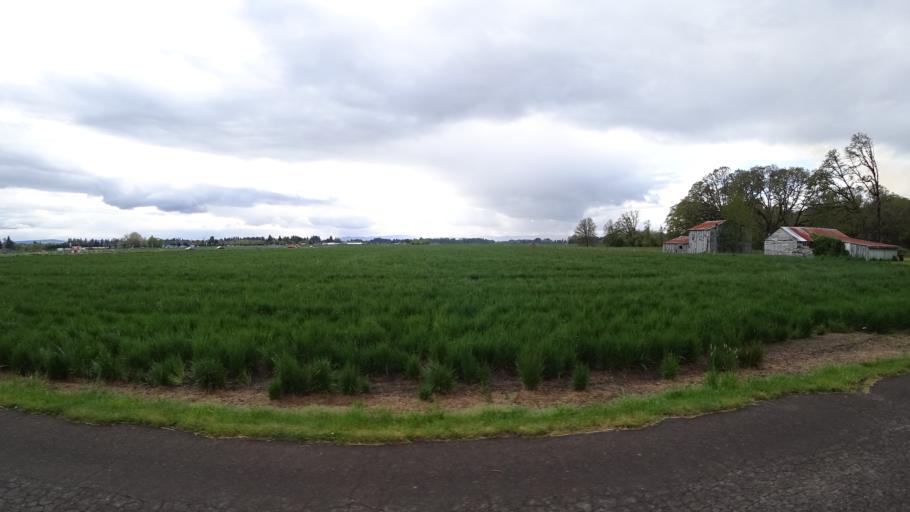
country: US
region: Oregon
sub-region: Washington County
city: Hillsboro
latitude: 45.5536
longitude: -122.9584
